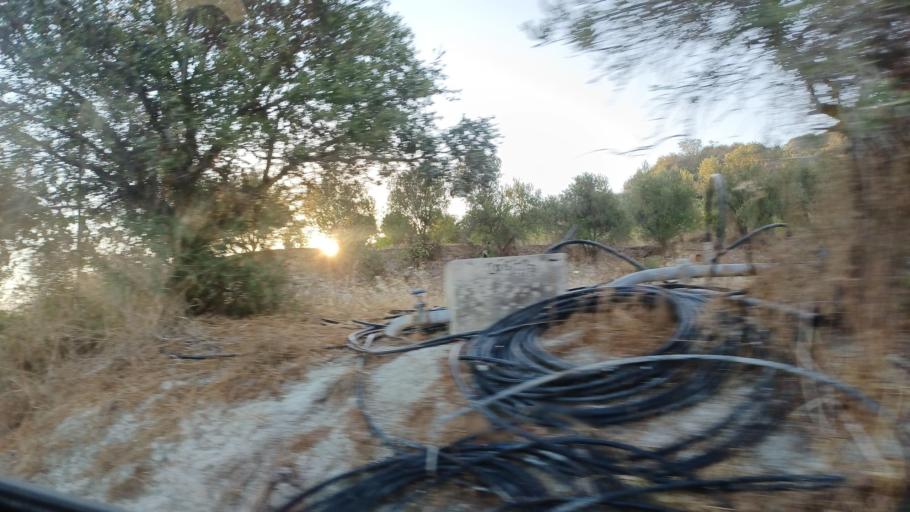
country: CY
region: Pafos
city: Polis
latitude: 35.0012
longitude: 32.4275
